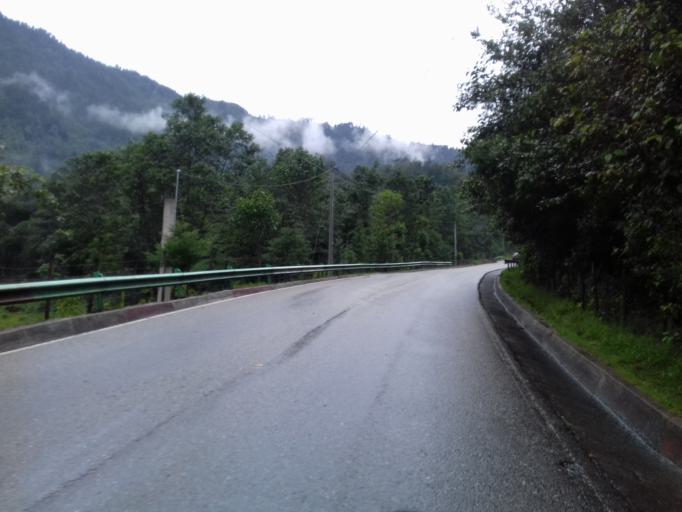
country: GT
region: Quiche
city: Nebaj
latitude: 15.3864
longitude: -91.1127
